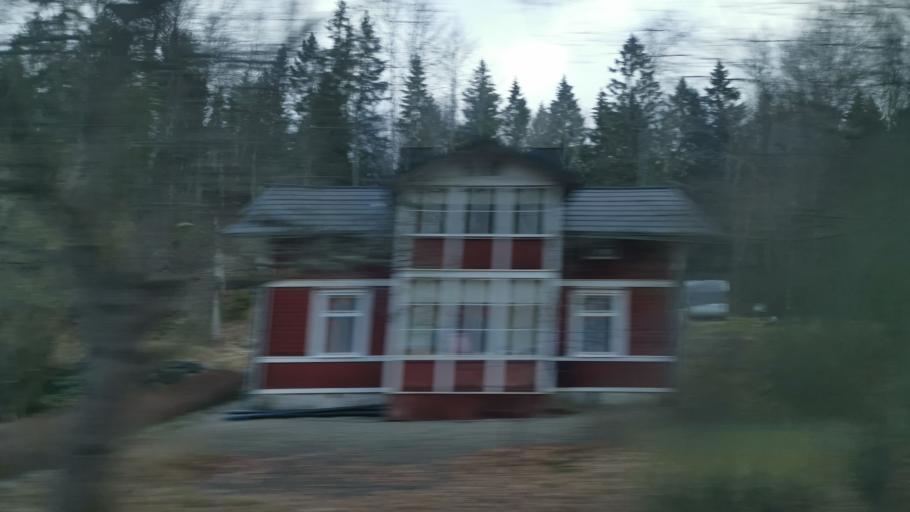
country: SE
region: Stockholm
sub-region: Sodertalje Kommun
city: Molnbo
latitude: 59.0504
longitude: 17.4344
